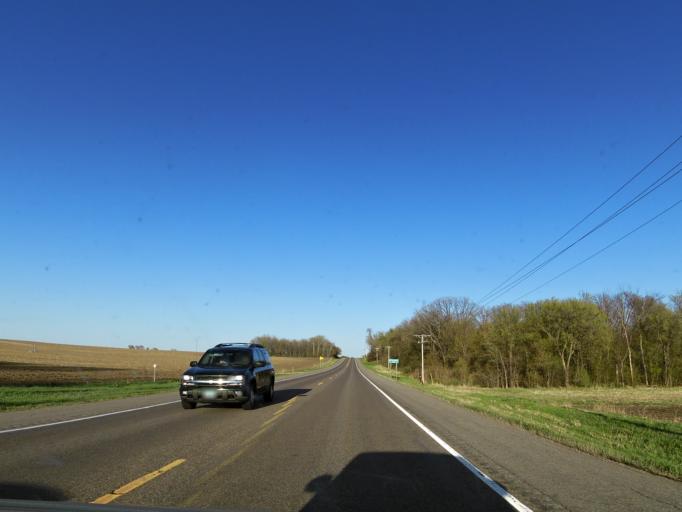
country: US
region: Minnesota
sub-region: Goodhue County
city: Cannon Falls
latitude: 44.6009
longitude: -92.8341
